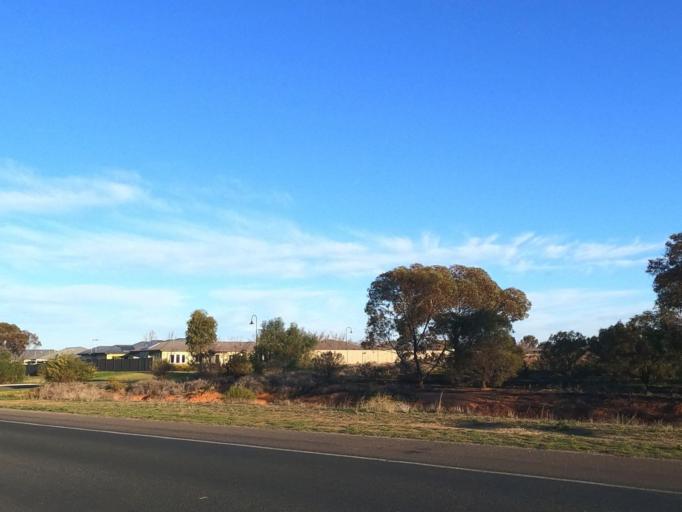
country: AU
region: Victoria
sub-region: Swan Hill
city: Swan Hill
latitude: -35.3347
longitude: 143.5318
